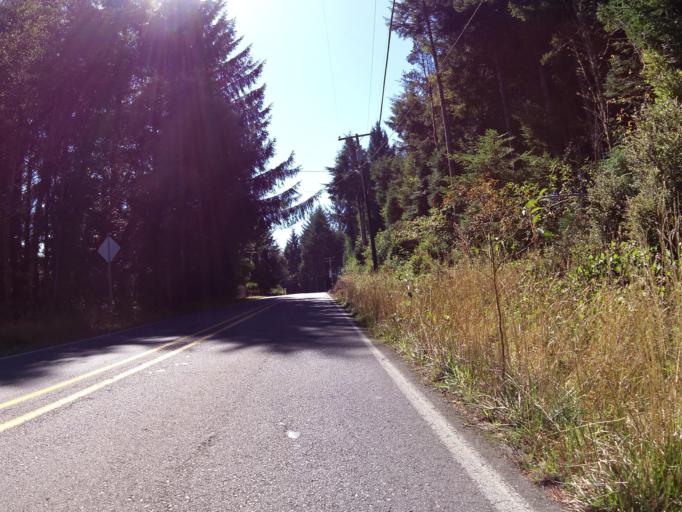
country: US
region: Oregon
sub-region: Coos County
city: Barview
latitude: 43.3285
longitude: -124.3410
